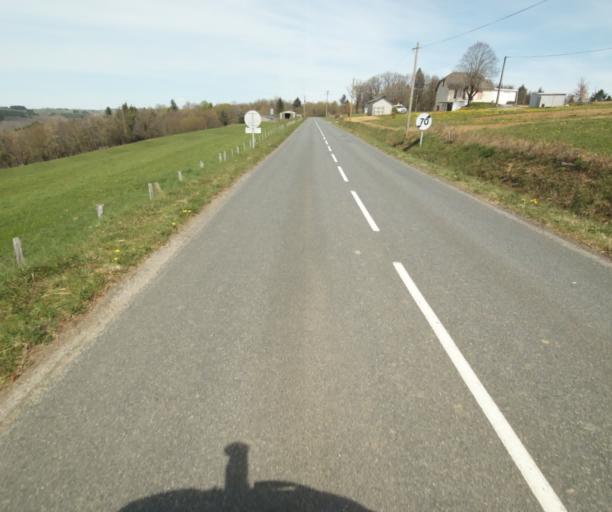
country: FR
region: Limousin
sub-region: Departement de la Correze
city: Naves
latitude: 45.3655
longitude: 1.7953
